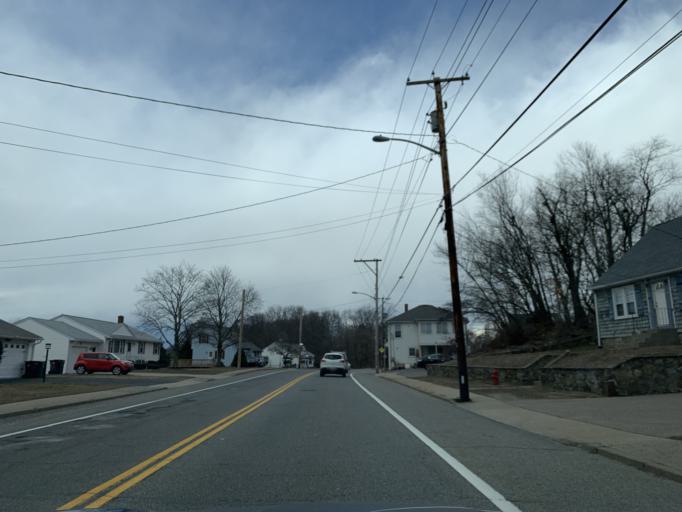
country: US
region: Rhode Island
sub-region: Providence County
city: Cumberland Hill
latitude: 41.9985
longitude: -71.4820
